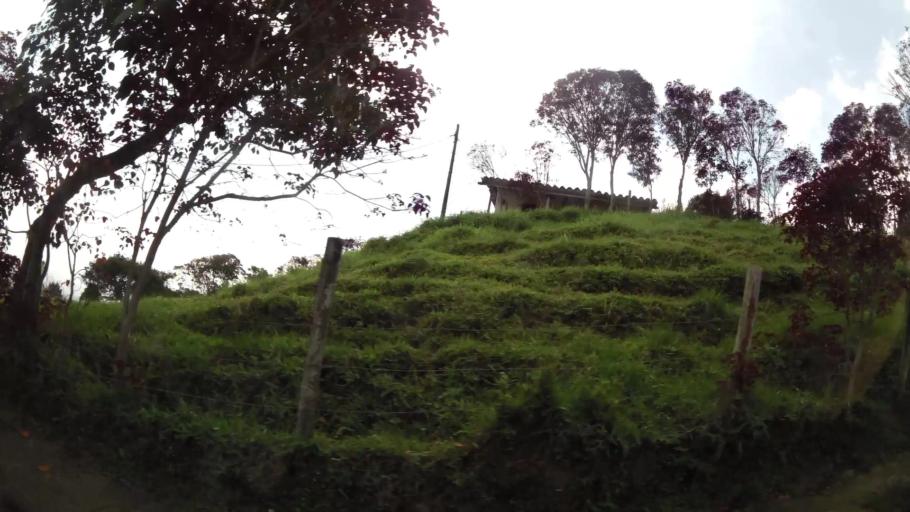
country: CO
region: Antioquia
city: La Estrella
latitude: 6.1726
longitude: -75.6536
